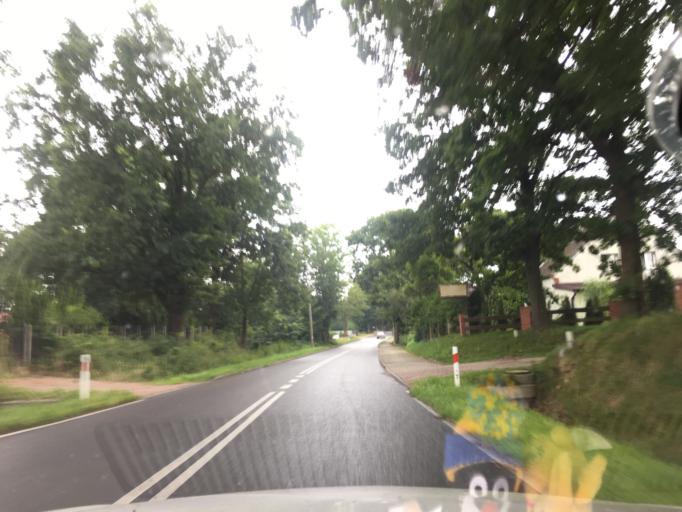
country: PL
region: West Pomeranian Voivodeship
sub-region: Powiat gryficki
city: Karnice
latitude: 54.0665
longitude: 15.0740
